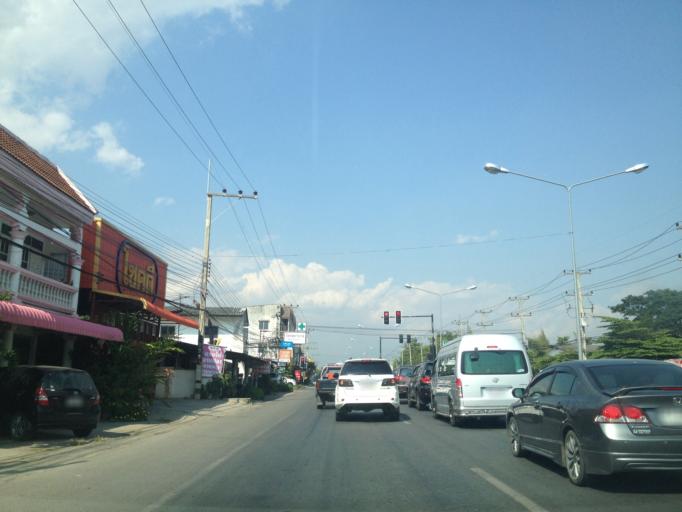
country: TH
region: Chiang Mai
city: San Pa Tong
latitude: 18.5948
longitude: 98.8889
